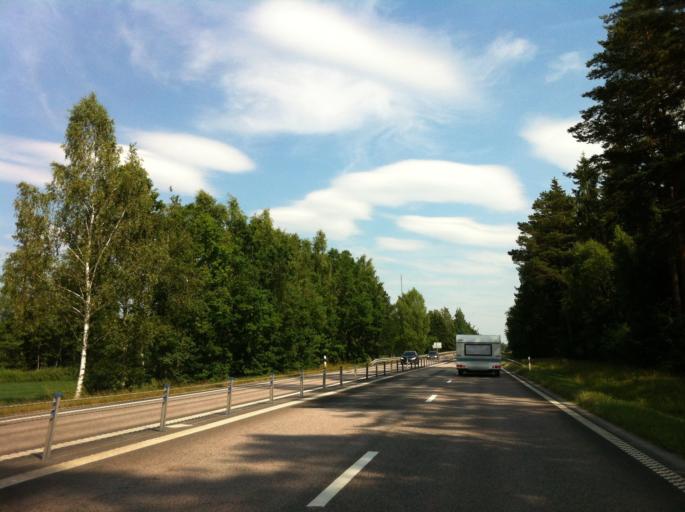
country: SE
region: Kalmar
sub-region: Nybro Kommun
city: Nybro
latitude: 56.7248
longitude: 16.0099
